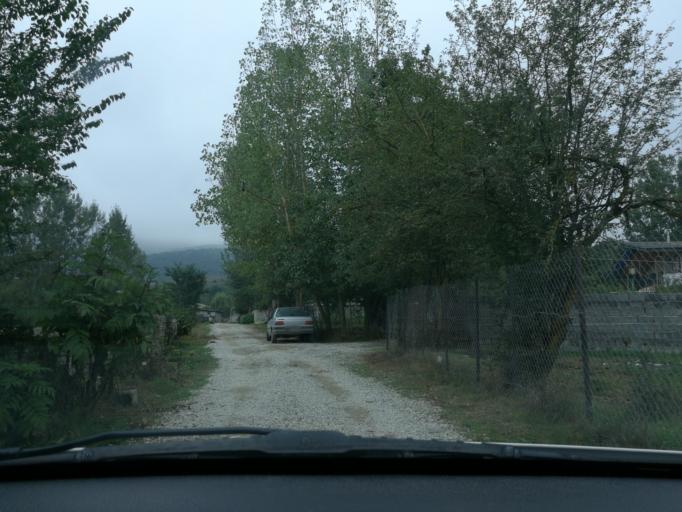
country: IR
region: Mazandaran
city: `Abbasabad
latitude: 36.4997
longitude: 51.2091
